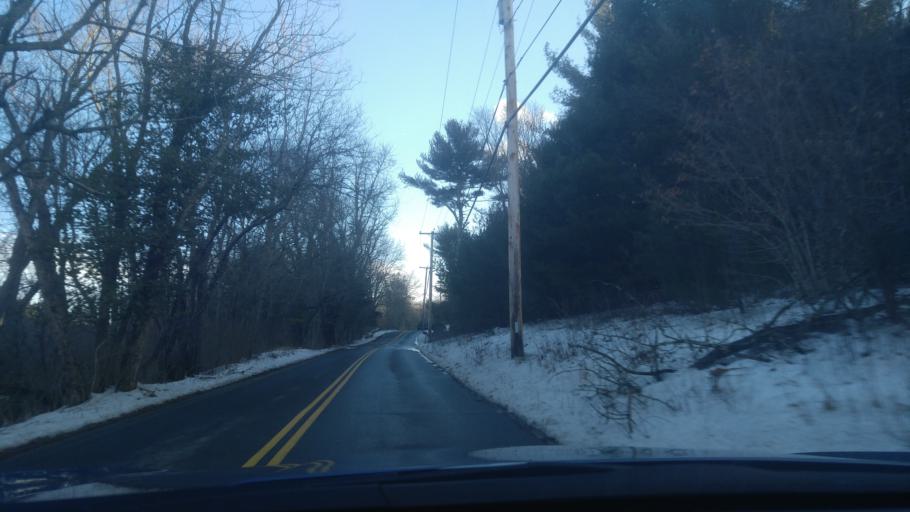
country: US
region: Rhode Island
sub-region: Kent County
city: Coventry
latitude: 41.7134
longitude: -71.6518
